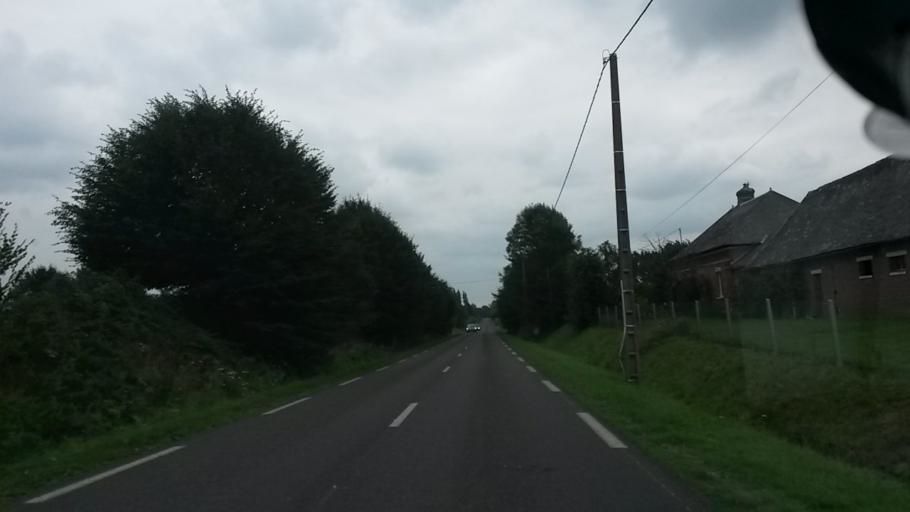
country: FR
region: Haute-Normandie
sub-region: Departement de la Seine-Maritime
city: Forges-les-Eaux
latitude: 49.5926
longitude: 1.5461
